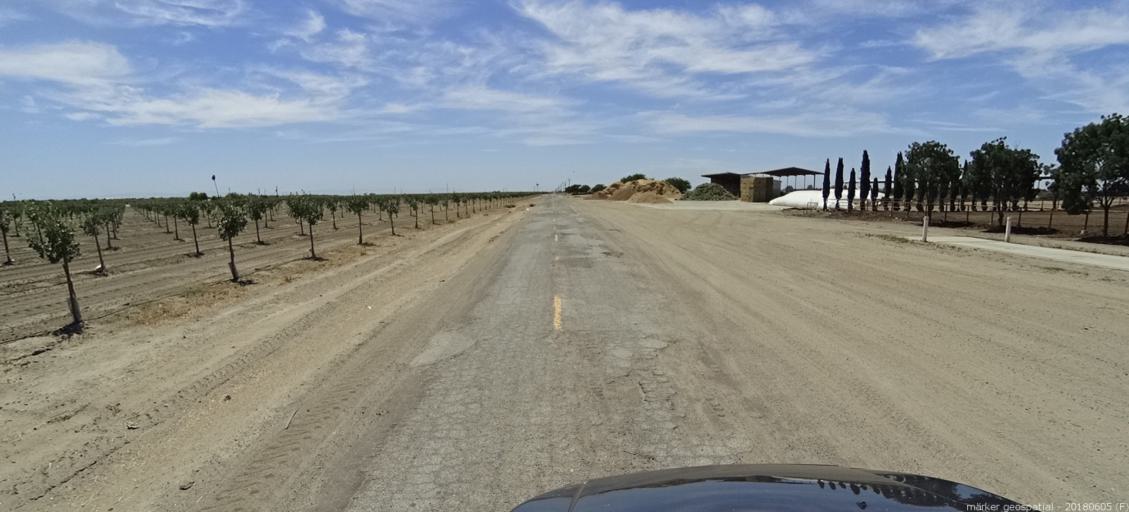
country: US
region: California
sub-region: Merced County
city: Dos Palos
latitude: 37.0907
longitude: -120.4613
